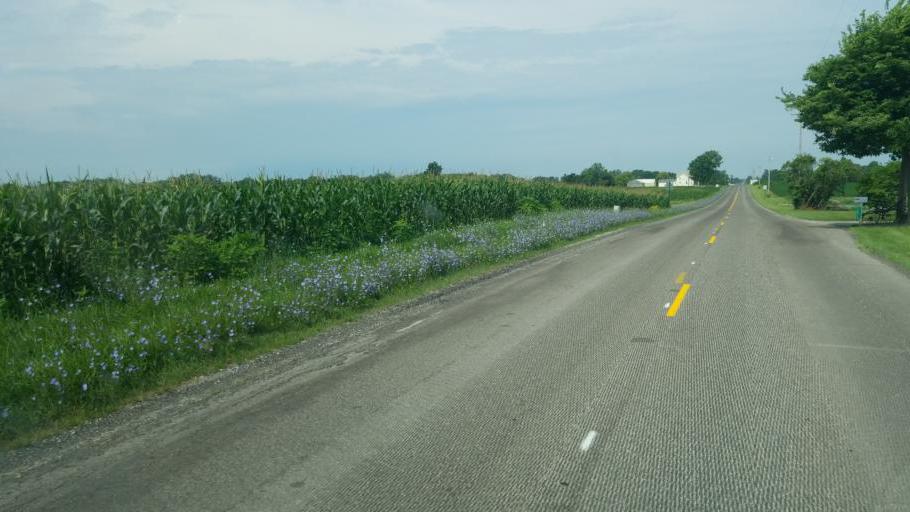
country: US
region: Ohio
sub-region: Wyandot County
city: Upper Sandusky
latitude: 40.8031
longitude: -83.3440
